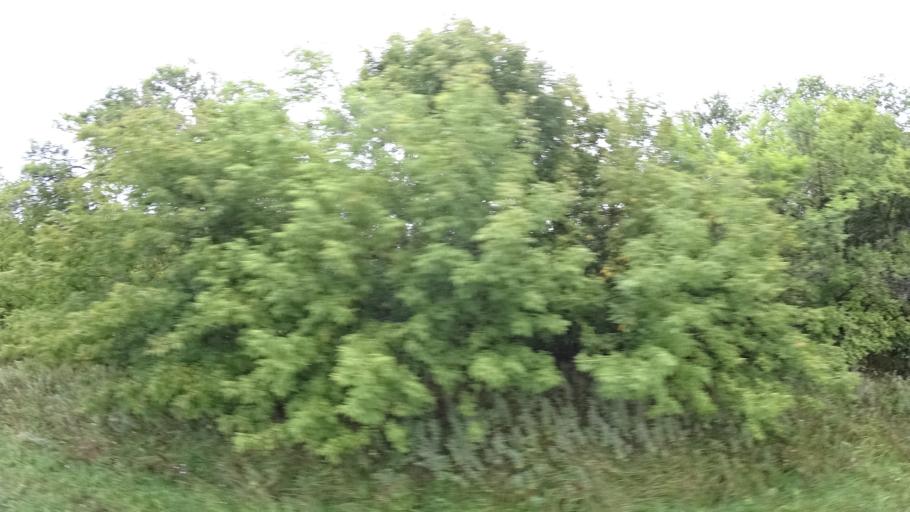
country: RU
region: Primorskiy
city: Monastyrishche
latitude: 44.2747
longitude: 132.4246
